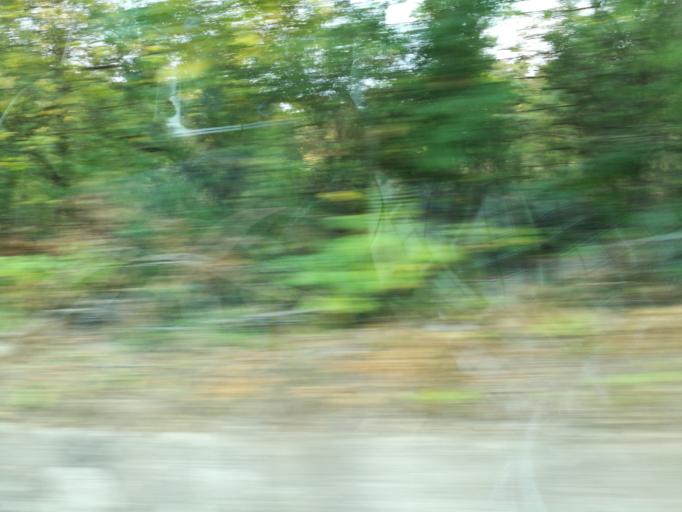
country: RO
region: Tulcea
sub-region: Comuna Horia
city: Horia
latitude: 45.0147
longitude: 28.4494
